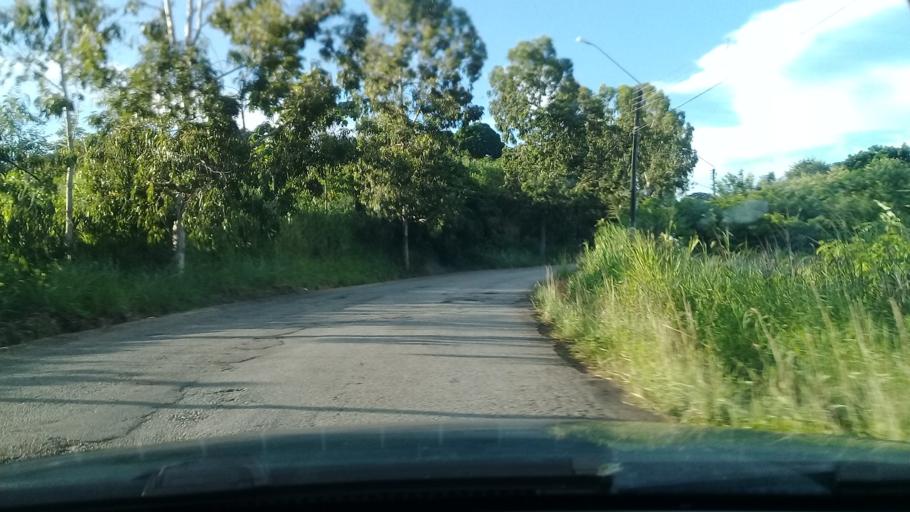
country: BR
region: Pernambuco
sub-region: Vicencia
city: Vicencia
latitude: -7.6129
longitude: -35.2353
